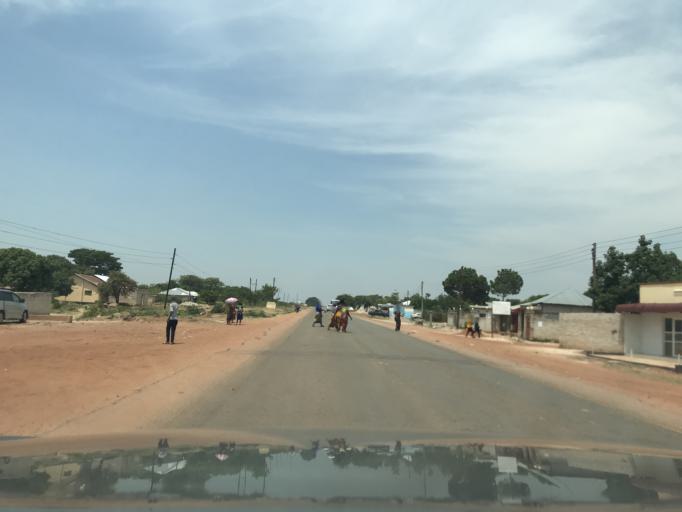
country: ZM
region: Northern
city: Kasama
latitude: -10.2145
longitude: 31.1530
